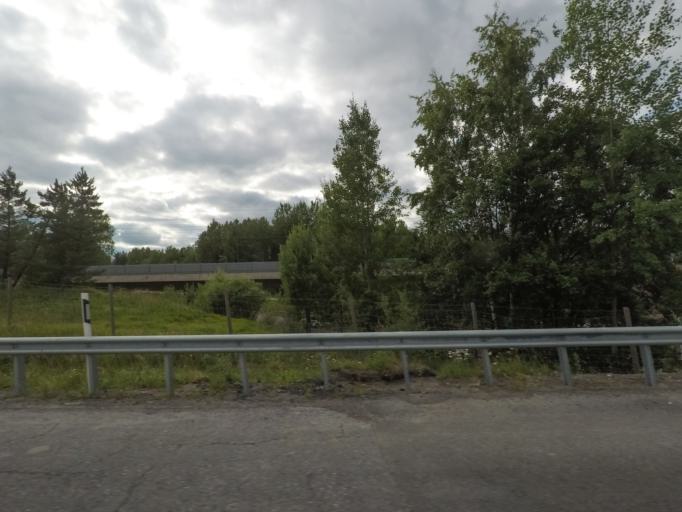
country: FI
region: Uusimaa
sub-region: Helsinki
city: Jaervenpaeae
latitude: 60.4710
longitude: 25.1374
